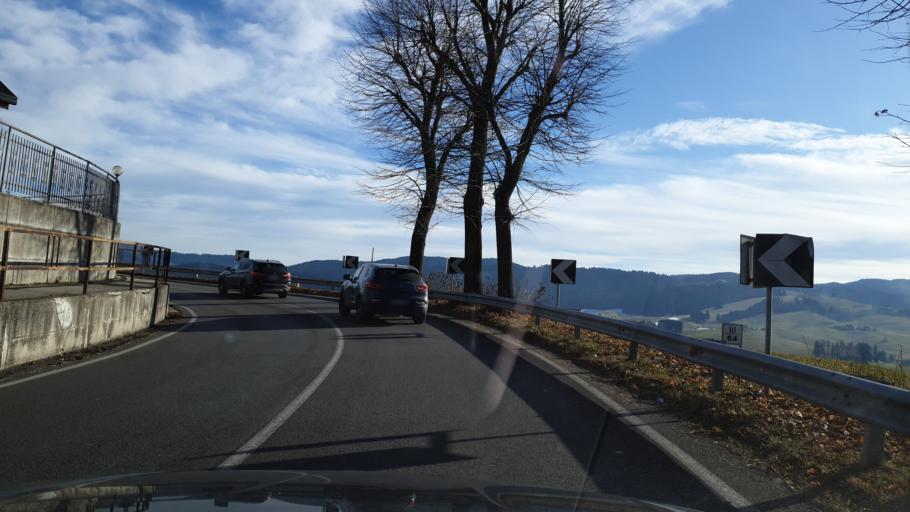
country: IT
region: Veneto
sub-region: Provincia di Vicenza
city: Canove di Roana
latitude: 45.8684
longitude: 11.4856
